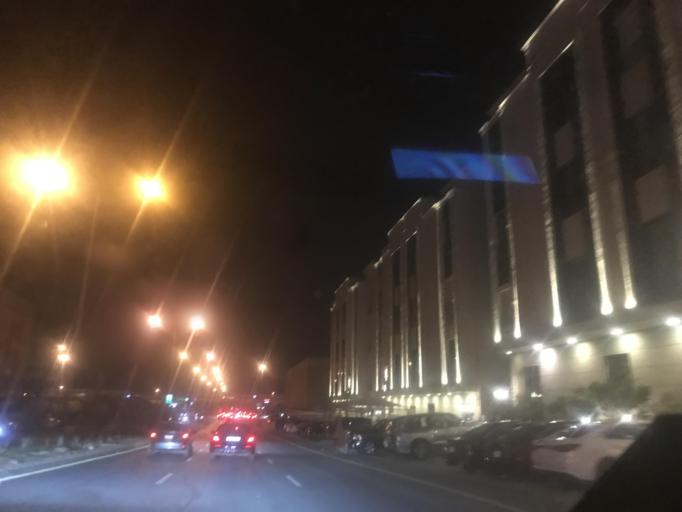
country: SA
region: Ar Riyad
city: Riyadh
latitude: 24.7678
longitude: 46.5795
